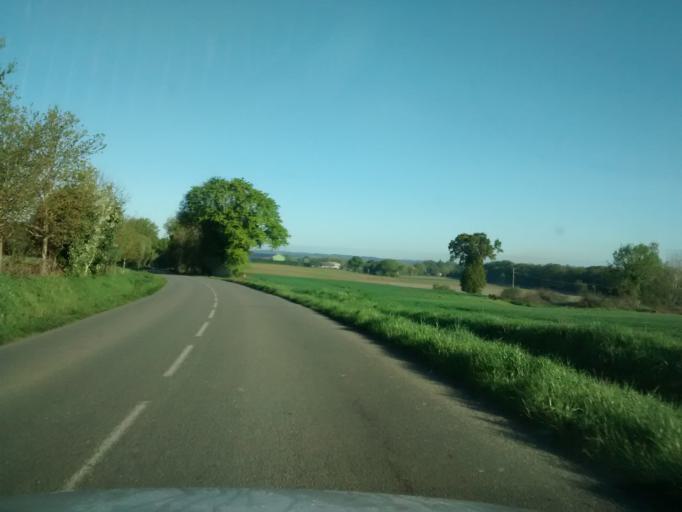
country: FR
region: Brittany
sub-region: Departement du Morbihan
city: Malestroit
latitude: 47.8217
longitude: -2.4023
